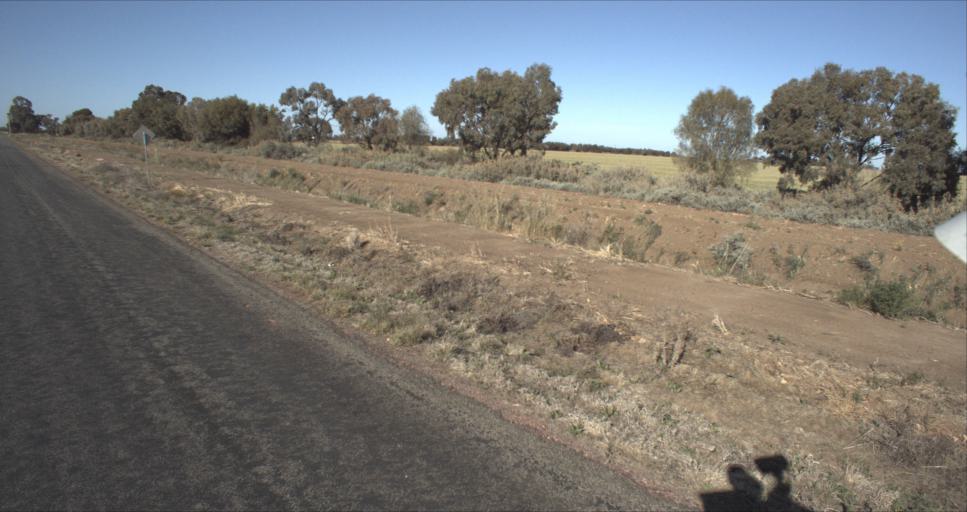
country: AU
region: New South Wales
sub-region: Leeton
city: Leeton
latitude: -34.5511
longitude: 146.2673
